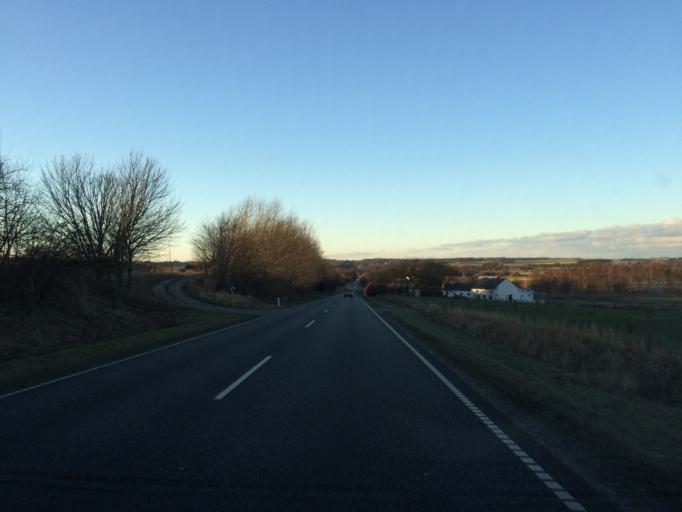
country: DK
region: Central Jutland
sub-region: Randers Kommune
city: Langa
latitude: 56.4852
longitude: 9.8691
